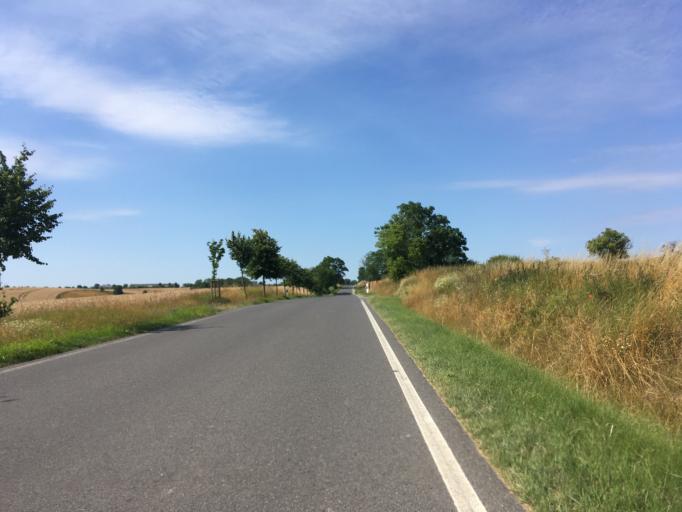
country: DE
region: Brandenburg
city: Gramzow
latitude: 53.2516
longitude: 14.0550
